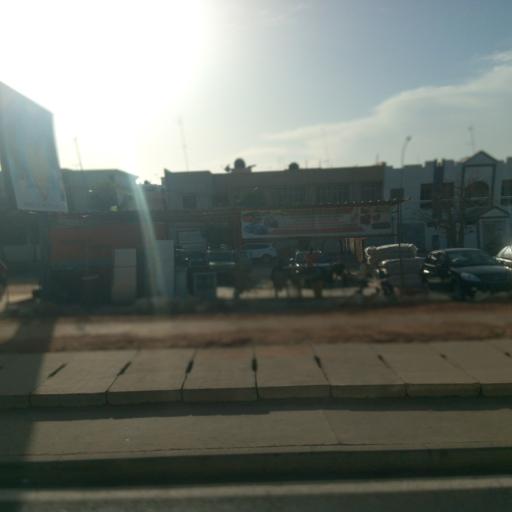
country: SN
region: Dakar
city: Mermoz Boabab
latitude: 14.7202
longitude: -17.4716
